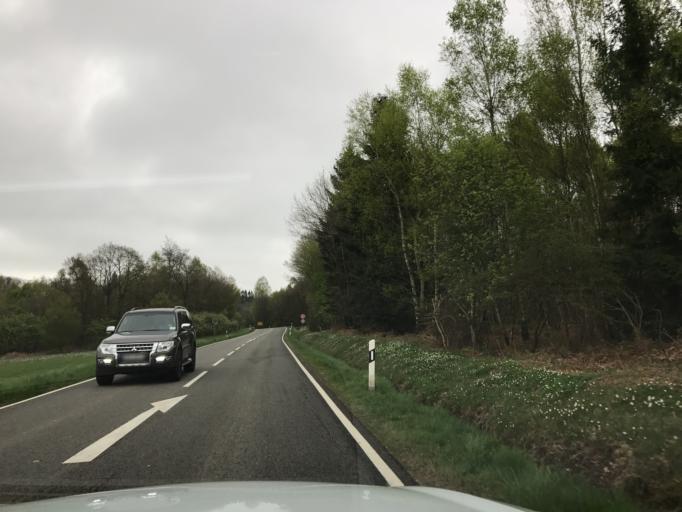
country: DE
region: Rheinland-Pfalz
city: Kirf
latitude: 49.5064
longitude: 6.4772
